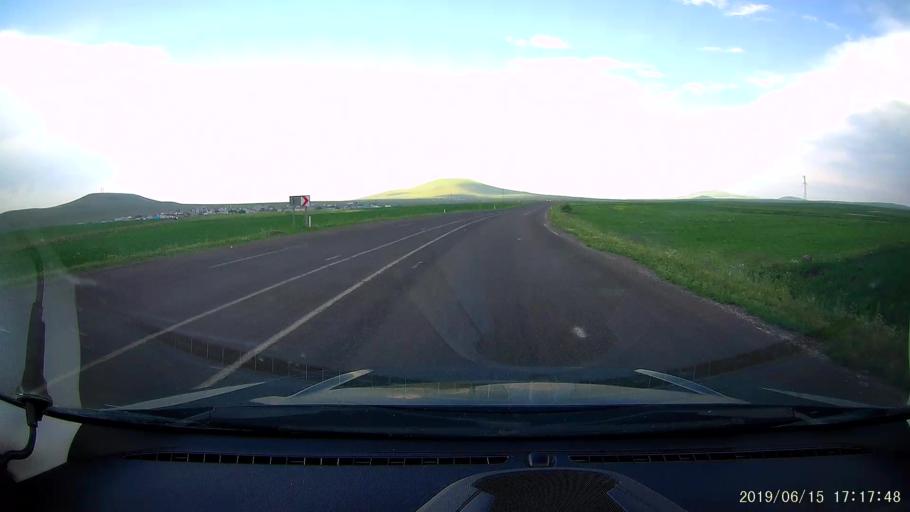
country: TR
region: Kars
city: Kars
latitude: 40.6149
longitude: 43.2458
